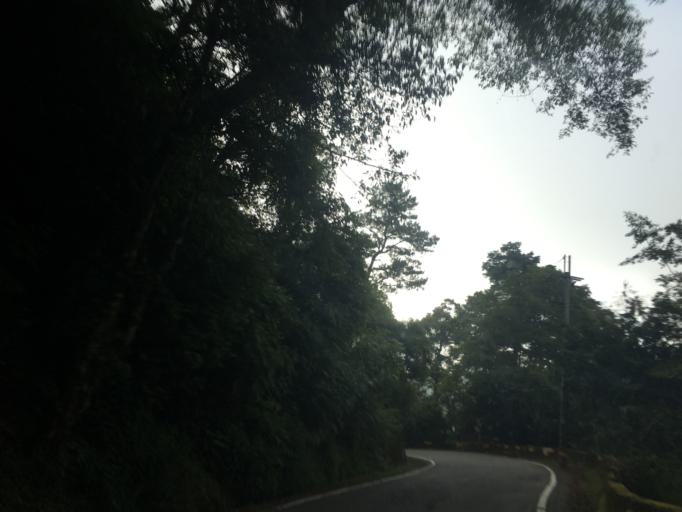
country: TW
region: Taiwan
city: Fengyuan
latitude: 24.2408
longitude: 120.9793
